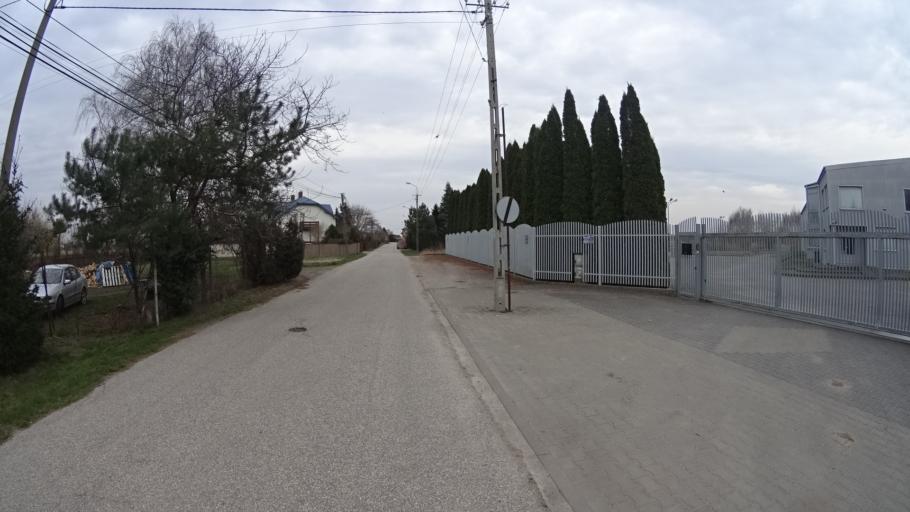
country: PL
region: Masovian Voivodeship
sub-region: Powiat warszawski zachodni
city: Jozefow
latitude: 52.2072
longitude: 20.6670
